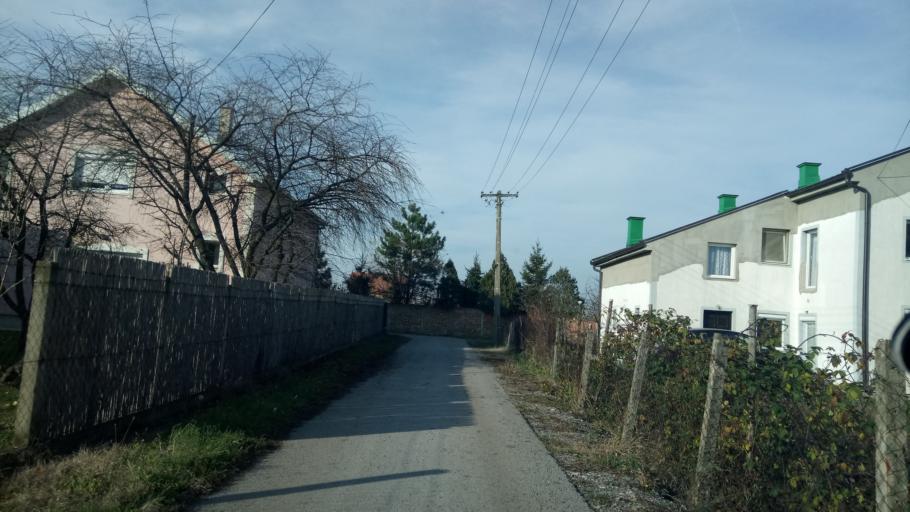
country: RS
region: Autonomna Pokrajina Vojvodina
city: Nova Pazova
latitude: 44.9543
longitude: 20.2216
